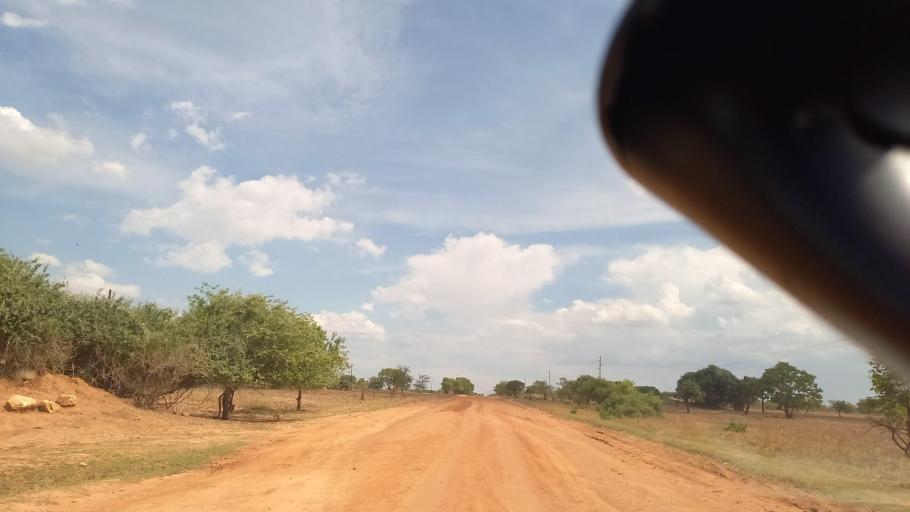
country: ZM
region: Lusaka
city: Kafue
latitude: -16.1349
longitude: 28.0499
